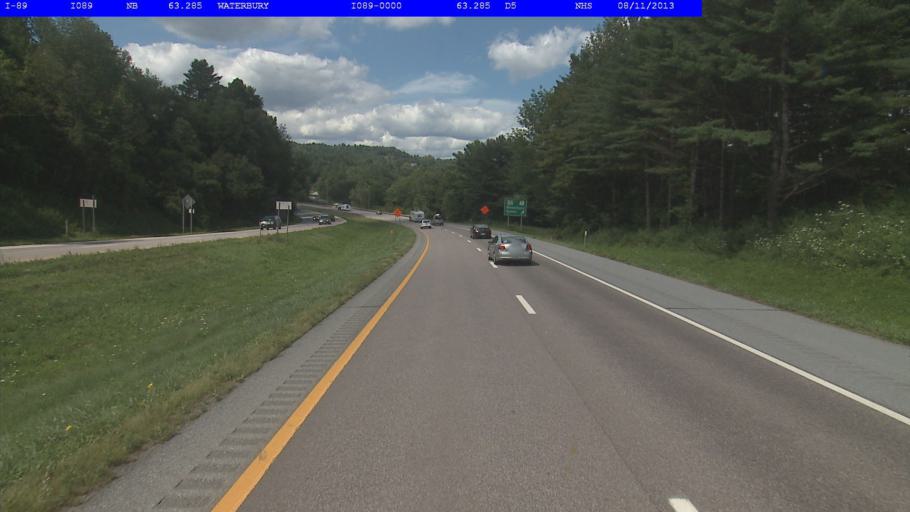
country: US
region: Vermont
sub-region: Washington County
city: Waterbury
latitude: 44.3379
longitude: -72.7469
